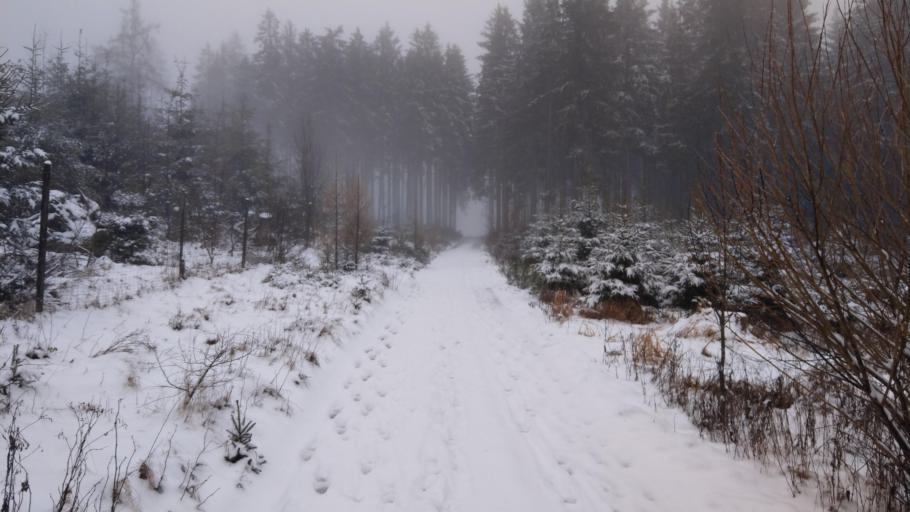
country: DE
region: North Rhine-Westphalia
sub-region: Regierungsbezirk Arnsberg
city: Erndtebruck
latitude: 50.9849
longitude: 8.2164
